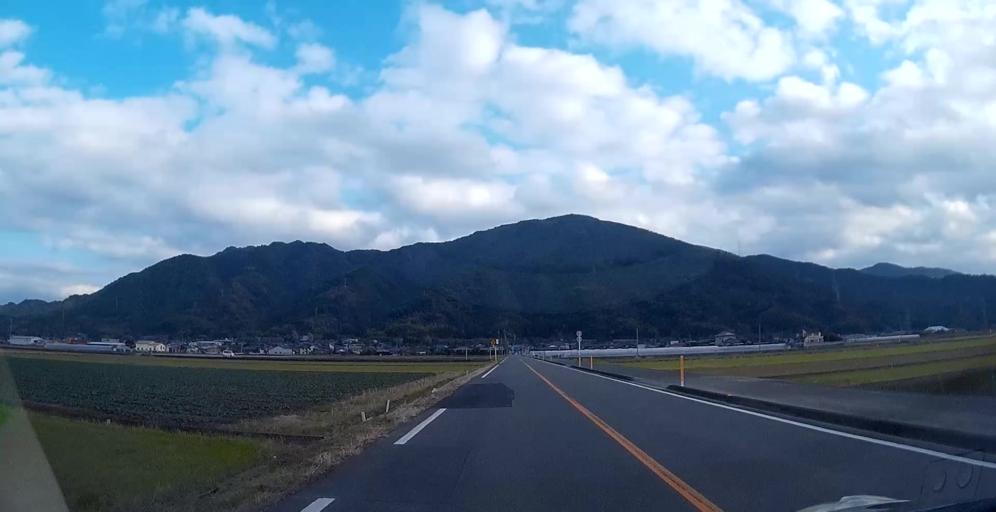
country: JP
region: Kumamoto
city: Yatsushiro
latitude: 32.5307
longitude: 130.6553
